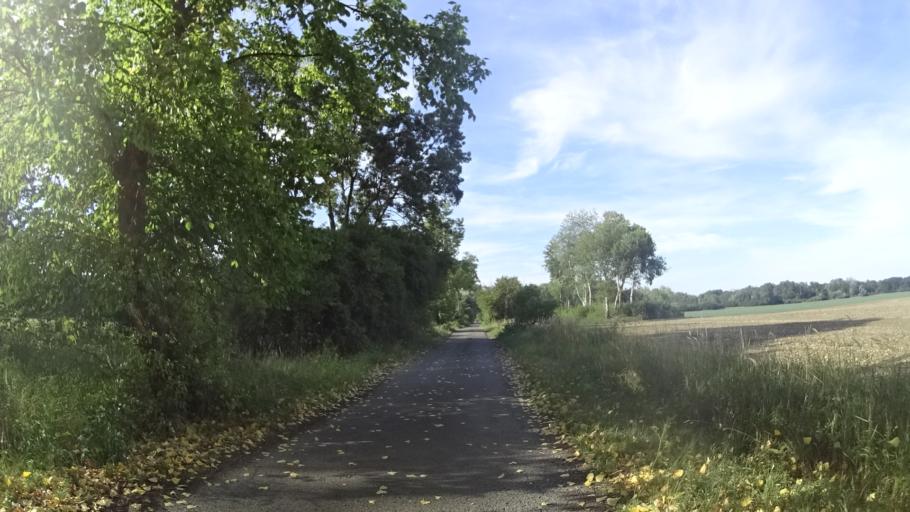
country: AT
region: Lower Austria
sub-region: Politischer Bezirk Ganserndorf
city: Drosing
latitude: 48.5914
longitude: 16.9506
